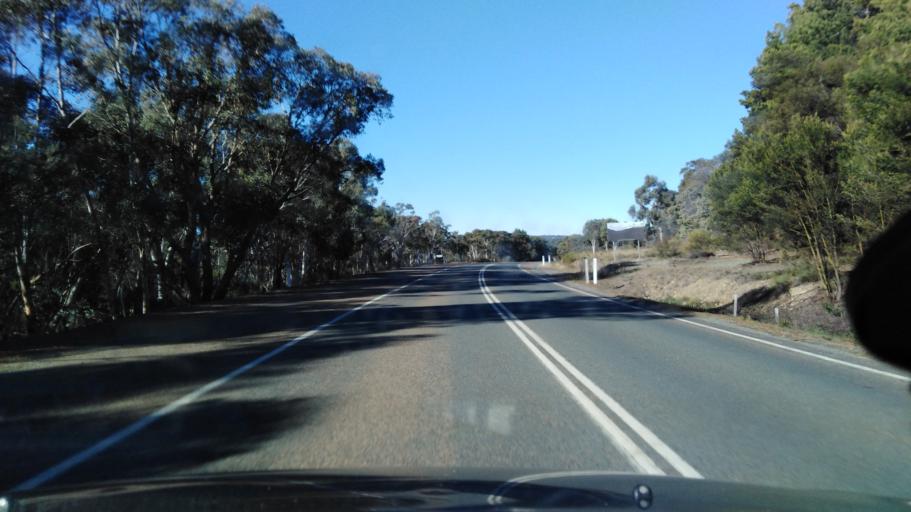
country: AU
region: New South Wales
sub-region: Palerang
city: Bungendore
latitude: -35.1871
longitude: 149.3233
